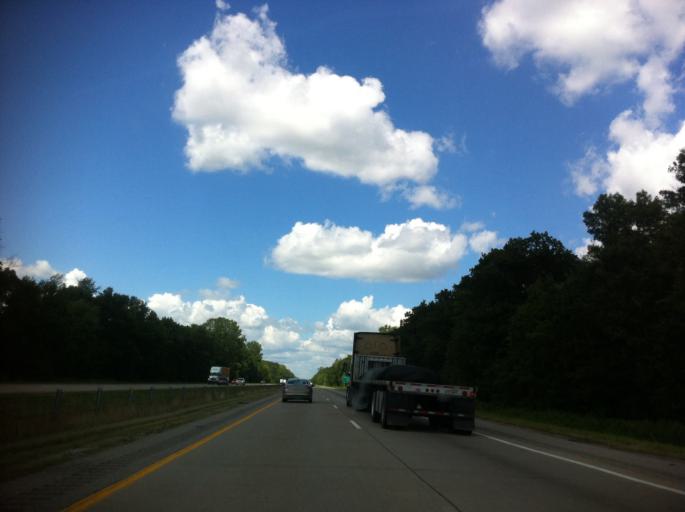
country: US
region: Michigan
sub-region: Monroe County
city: Petersburg
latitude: 41.8887
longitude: -83.6613
